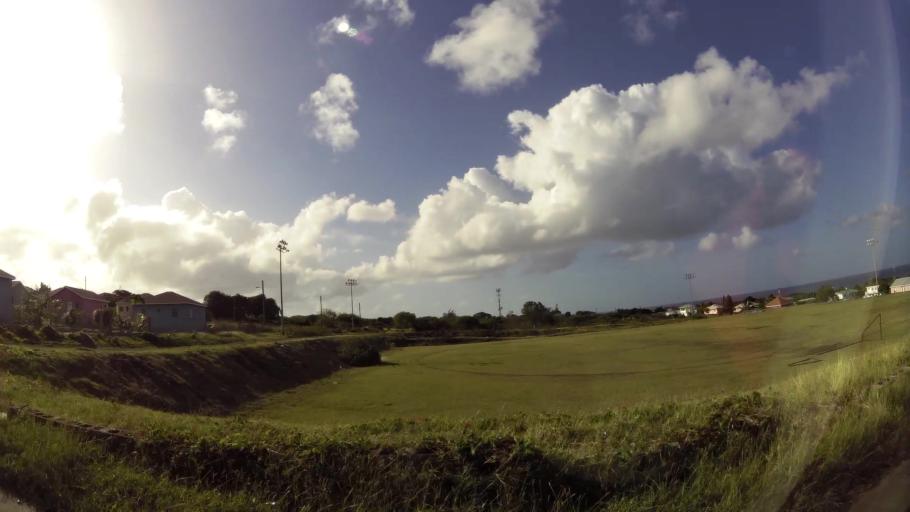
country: KN
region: Saint Paul Charlestown
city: Charlestown
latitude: 17.1420
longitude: -62.6217
